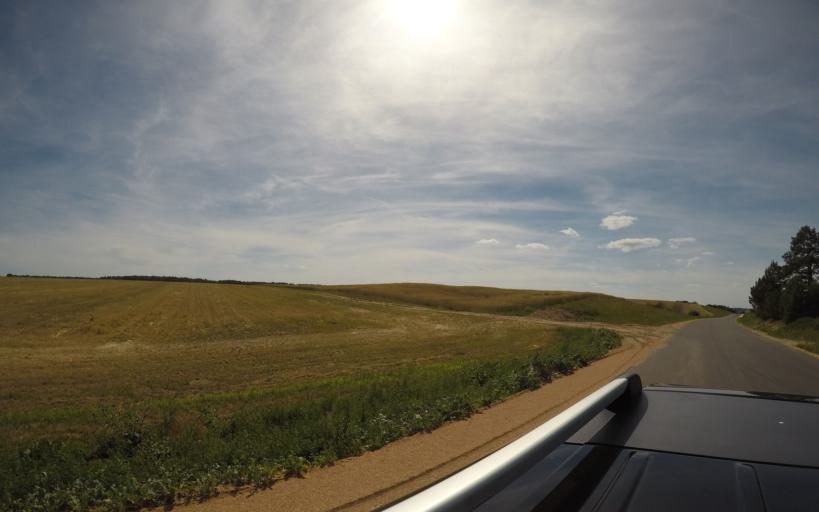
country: BY
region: Grodnenskaya
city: Hal'shany
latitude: 54.2581
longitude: 25.9813
